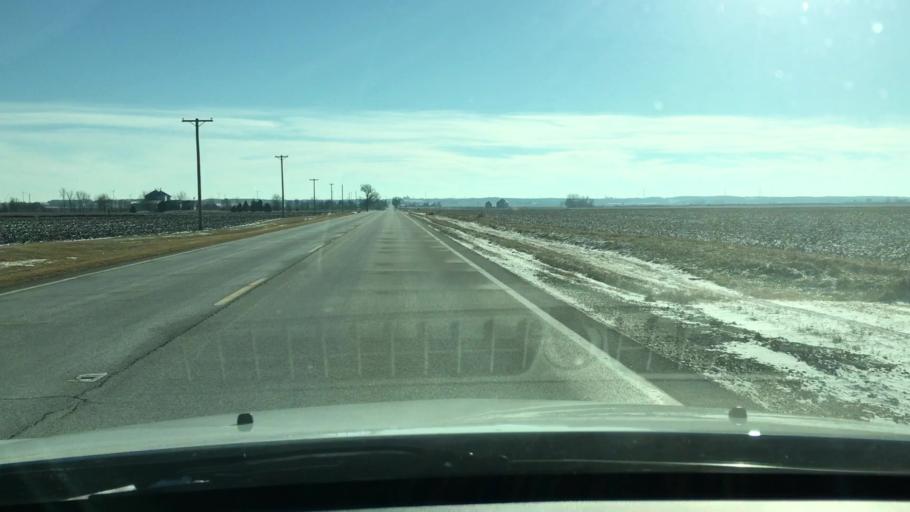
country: US
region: Illinois
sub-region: Ogle County
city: Rochelle
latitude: 41.7812
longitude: -89.0836
